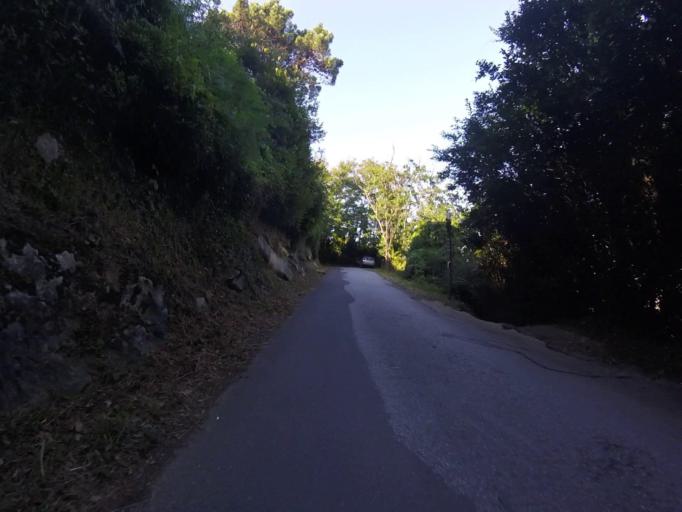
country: ES
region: Basque Country
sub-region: Provincia de Guipuzcoa
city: Fuenterrabia
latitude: 43.3898
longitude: -1.7900
